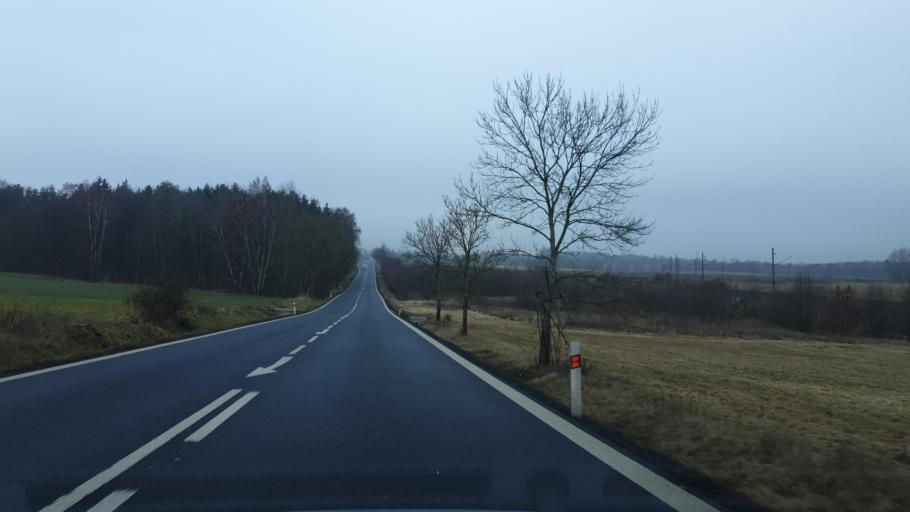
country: CZ
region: Karlovarsky
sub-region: Okres Cheb
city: Skalna
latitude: 50.1577
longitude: 12.3229
